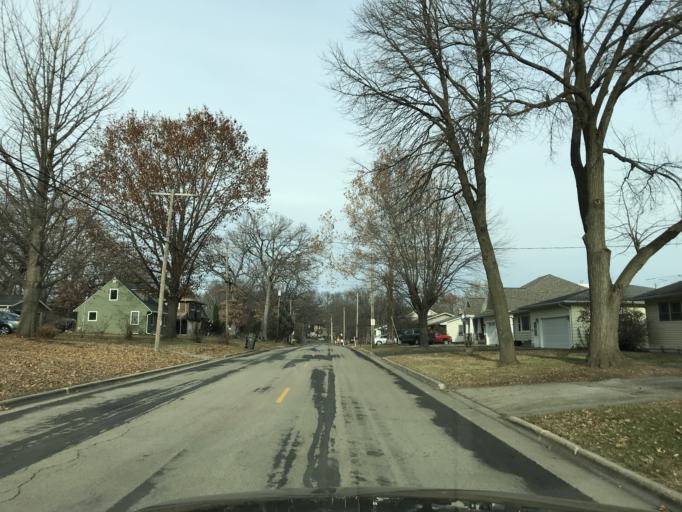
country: US
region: Wisconsin
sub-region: Dane County
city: Monona
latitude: 43.0630
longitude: -89.3454
